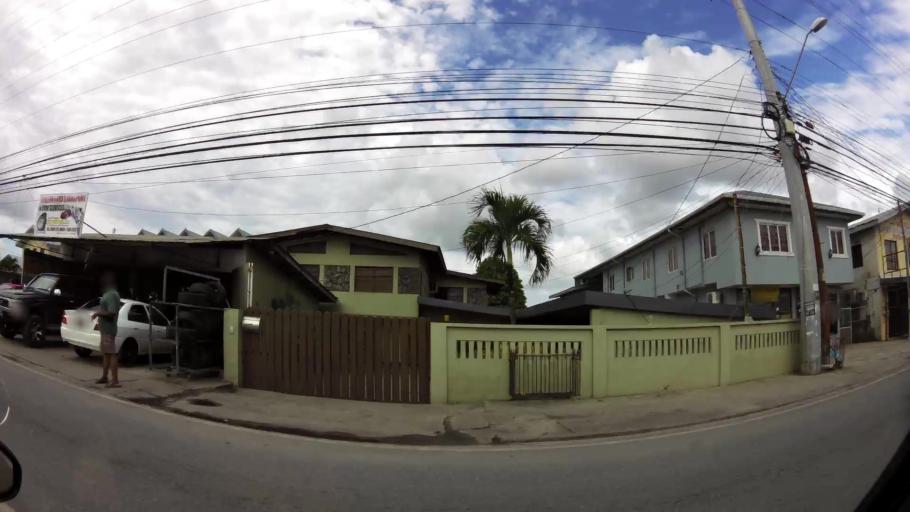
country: TT
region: Chaguanas
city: Chaguanas
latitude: 10.5069
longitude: -61.4074
